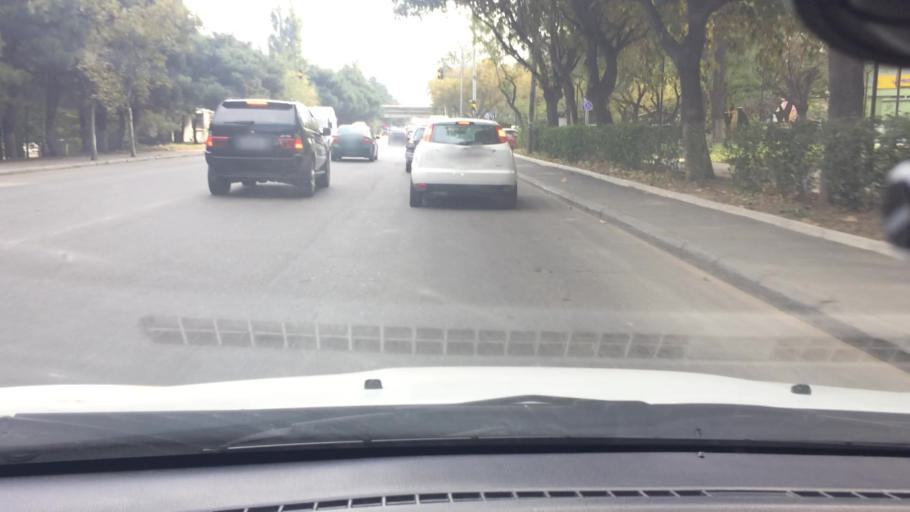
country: GE
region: T'bilisi
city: Tbilisi
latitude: 41.6455
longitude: 44.9111
